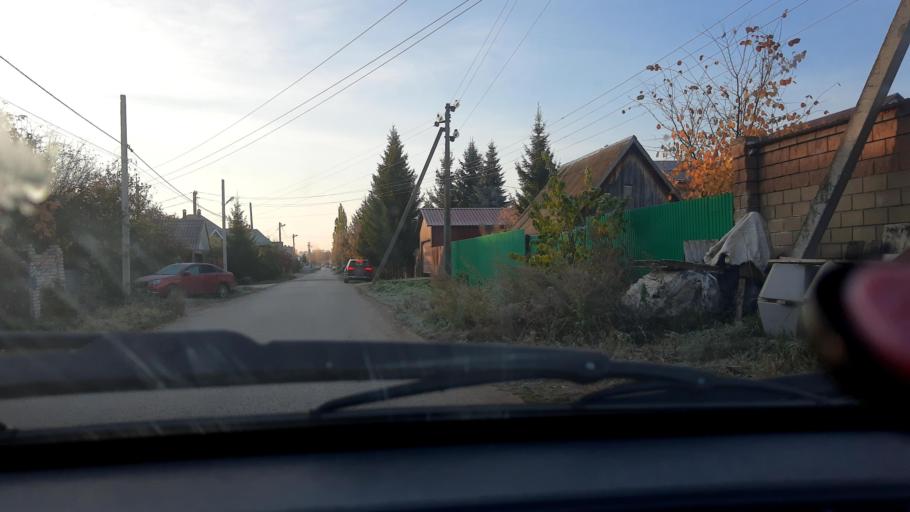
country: RU
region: Bashkortostan
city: Mikhaylovka
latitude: 54.7881
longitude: 55.8985
